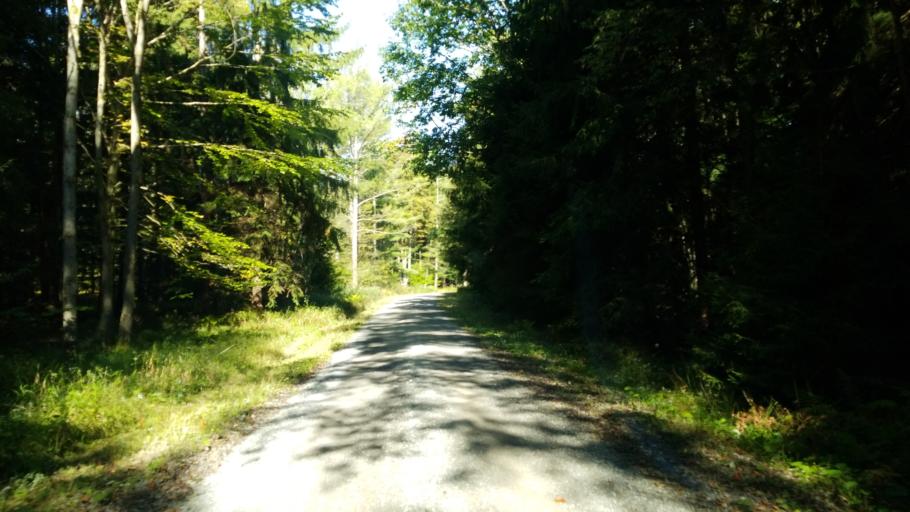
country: US
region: Pennsylvania
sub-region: Clearfield County
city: Treasure Lake
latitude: 41.1364
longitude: -78.5704
